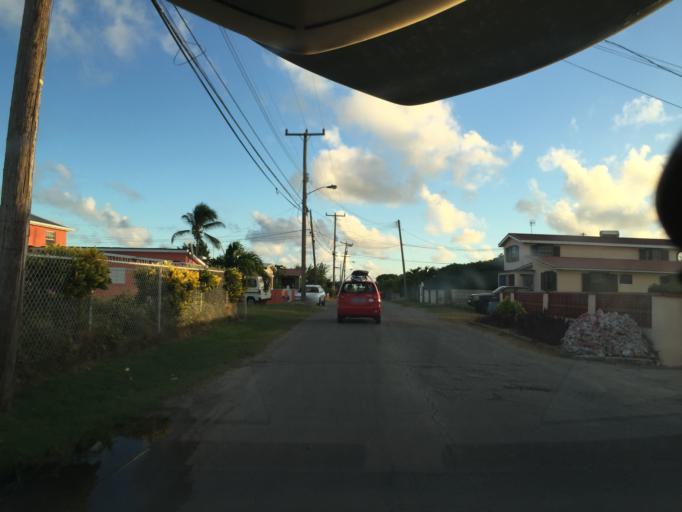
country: BB
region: Christ Church
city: Oistins
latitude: 13.0569
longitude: -59.5110
